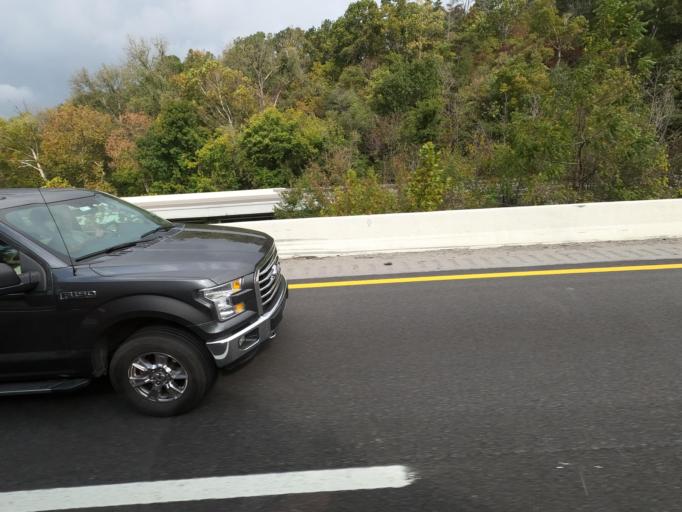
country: US
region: Tennessee
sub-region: Dickson County
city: White Bluff
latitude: 36.0300
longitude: -87.2089
